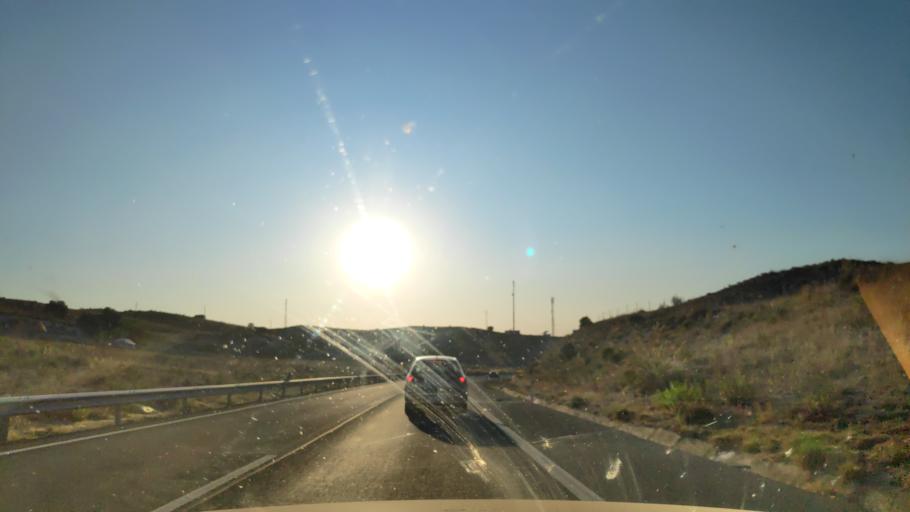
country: ES
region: Madrid
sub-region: Provincia de Madrid
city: Tielmes
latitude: 40.1986
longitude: -3.3106
